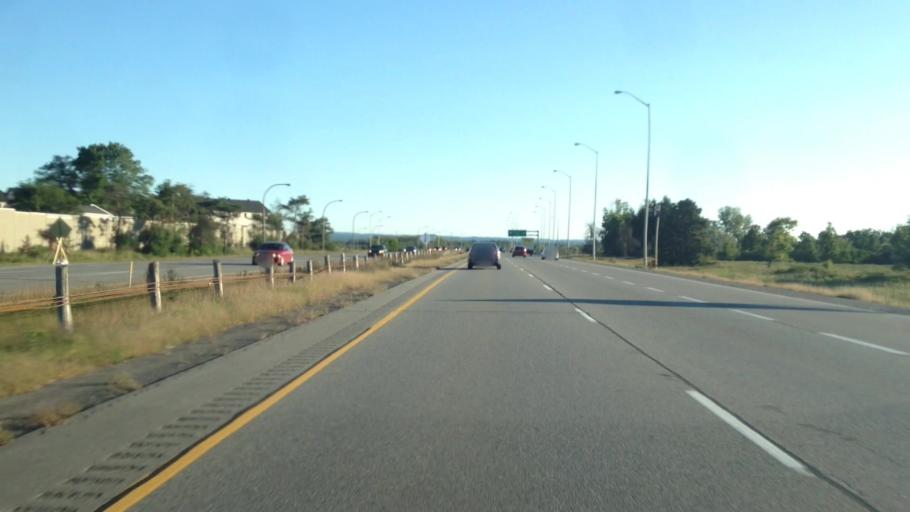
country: CA
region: Ontario
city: Ottawa
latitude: 45.4465
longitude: -75.5869
